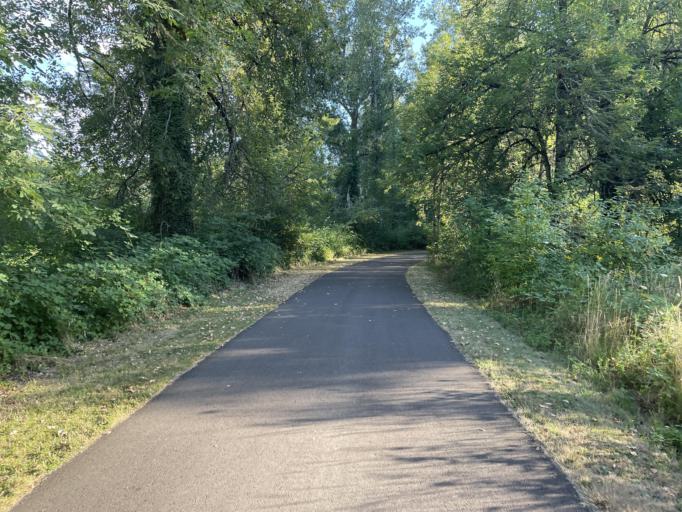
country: US
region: Oregon
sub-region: Marion County
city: Salem
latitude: 44.9175
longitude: -123.0784
